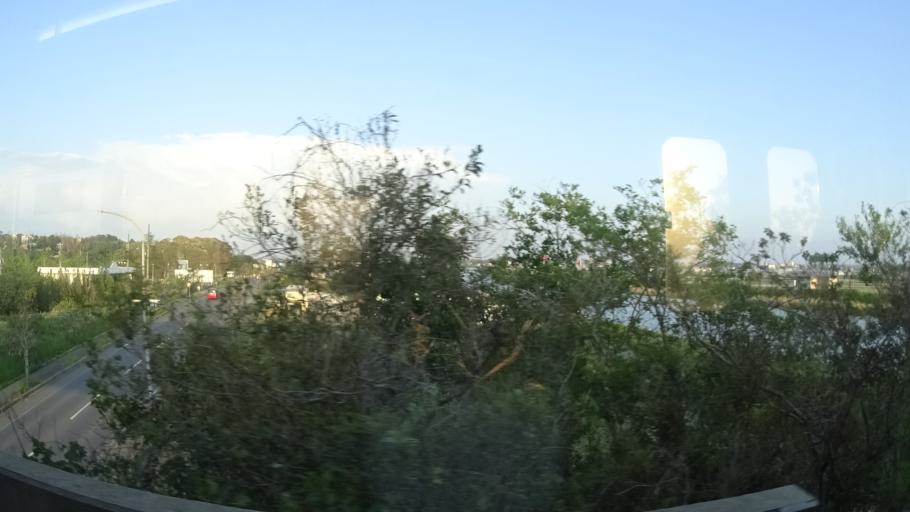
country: JP
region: Aichi
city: Toyohashi
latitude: 34.7163
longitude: 137.3787
